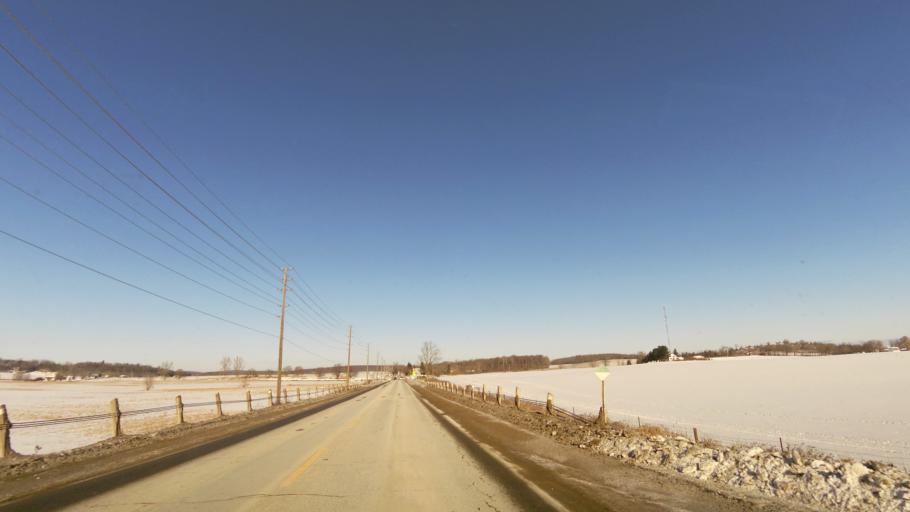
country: CA
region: Ontario
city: Quinte West
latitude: 44.2085
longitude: -77.8235
